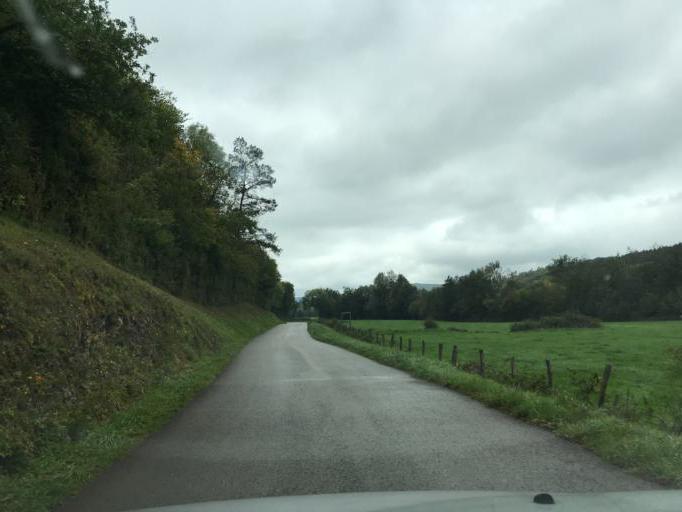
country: FR
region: Franche-Comte
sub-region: Departement du Jura
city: Arinthod
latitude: 46.4416
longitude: 5.4962
